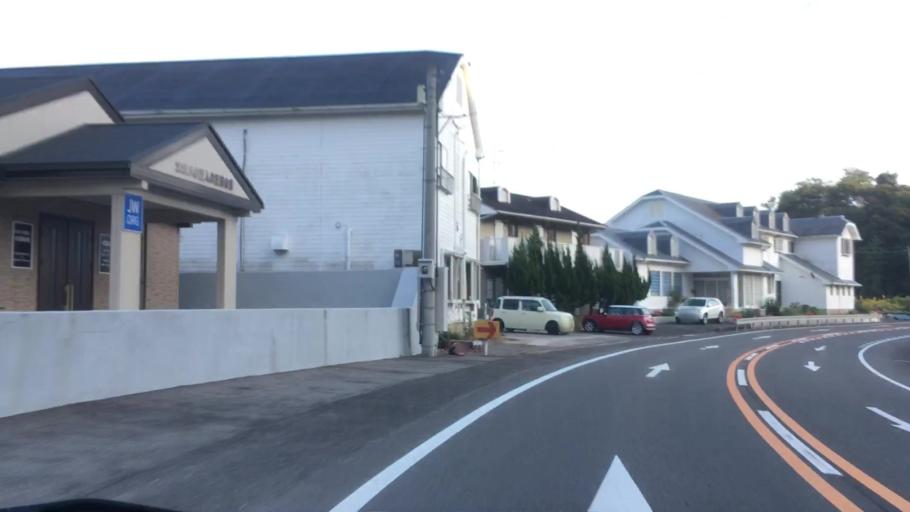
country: JP
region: Nagasaki
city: Sasebo
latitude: 33.0138
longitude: 129.7344
